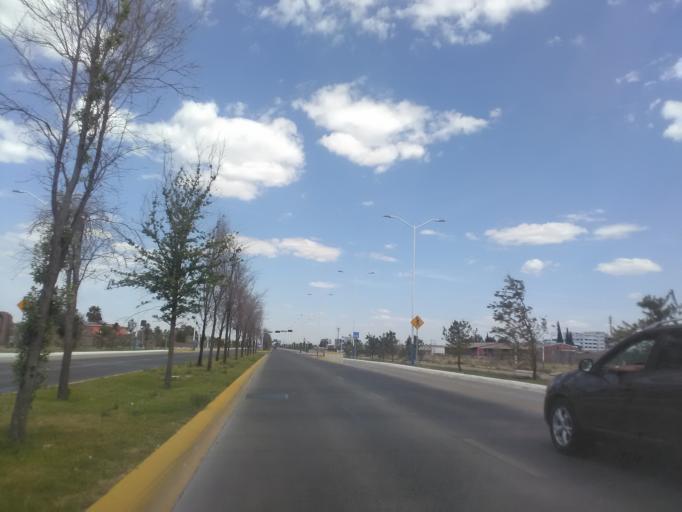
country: MX
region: Durango
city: Victoria de Durango
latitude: 24.0366
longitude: -104.6676
